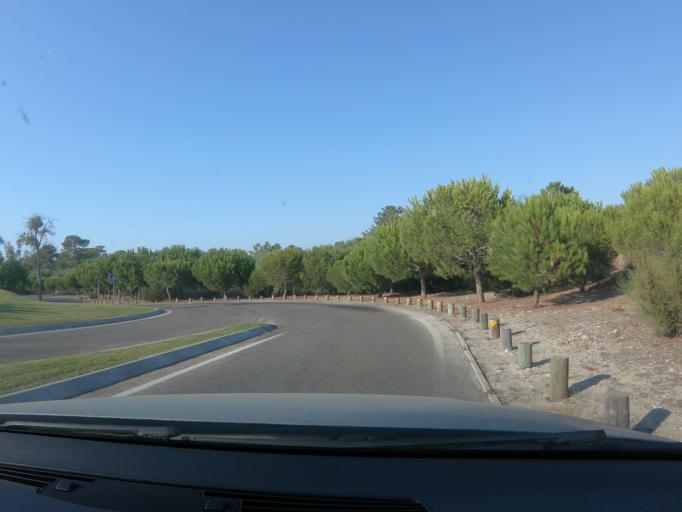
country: PT
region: Setubal
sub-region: Setubal
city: Setubal
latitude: 38.4872
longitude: -8.8962
